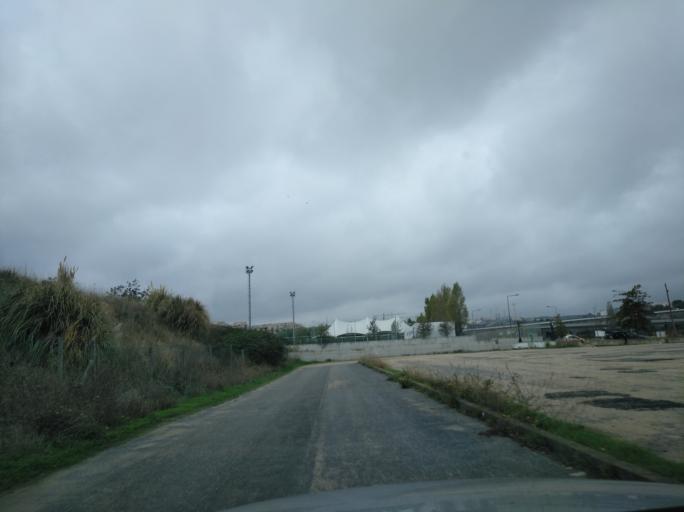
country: PT
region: Lisbon
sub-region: Loures
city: Bobadela
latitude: 38.7944
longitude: -9.0939
